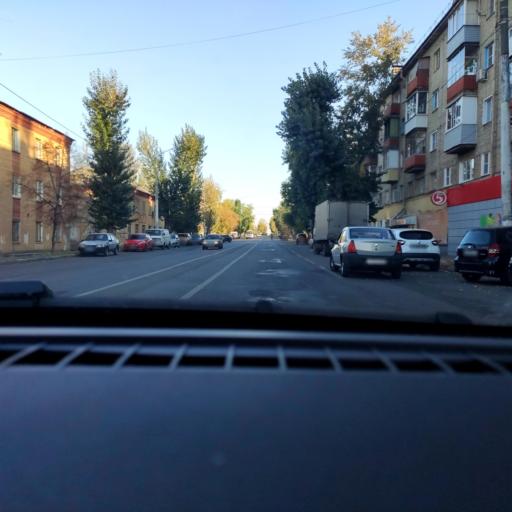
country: RU
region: Voronezj
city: Maslovka
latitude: 51.6205
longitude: 39.2462
